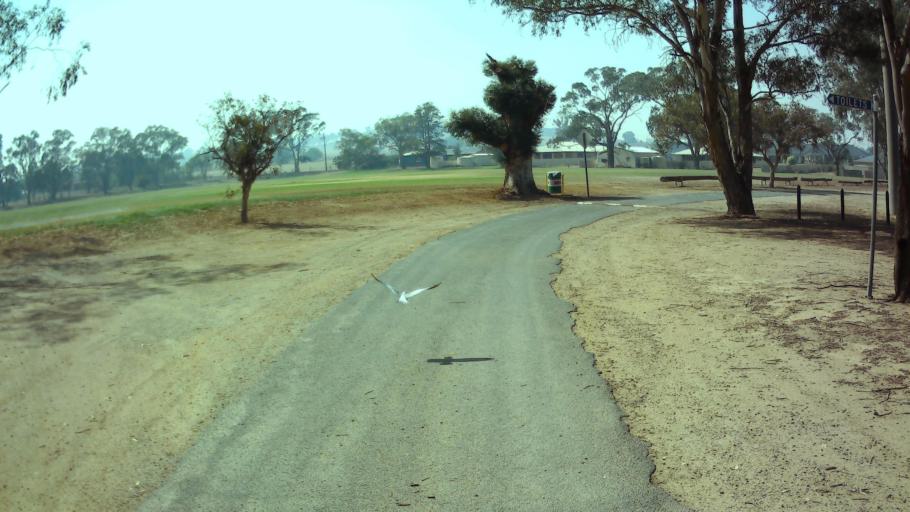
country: AU
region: New South Wales
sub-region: Weddin
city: Grenfell
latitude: -33.9057
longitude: 148.1623
